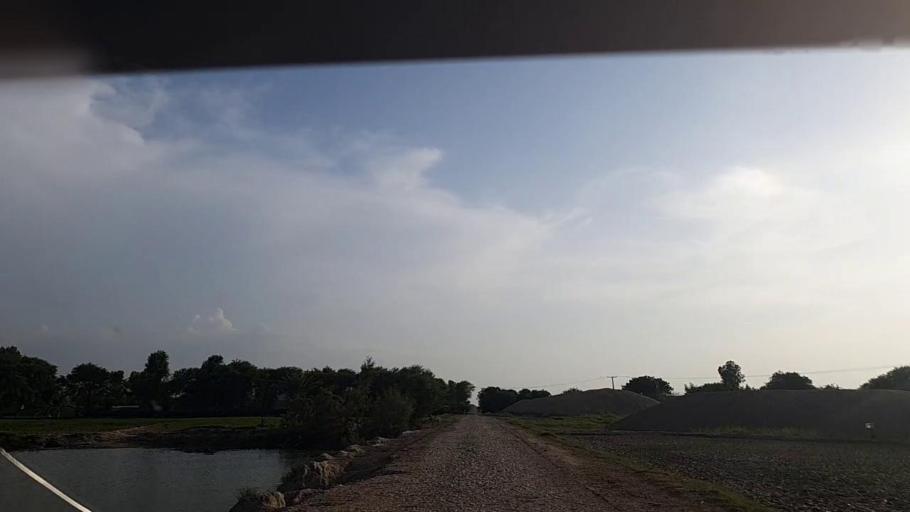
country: PK
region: Sindh
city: Khanpur
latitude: 27.8079
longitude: 69.3374
